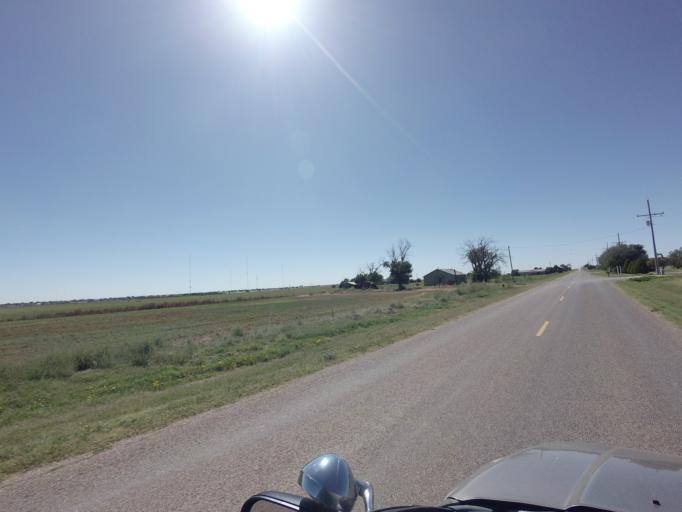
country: US
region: New Mexico
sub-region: Curry County
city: Clovis
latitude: 34.4484
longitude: -103.2047
